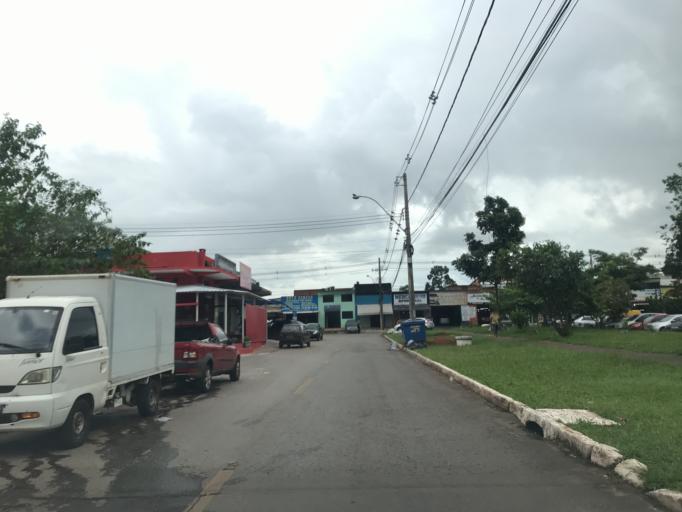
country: BR
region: Federal District
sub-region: Brasilia
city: Brasilia
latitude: -15.7874
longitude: -47.9179
